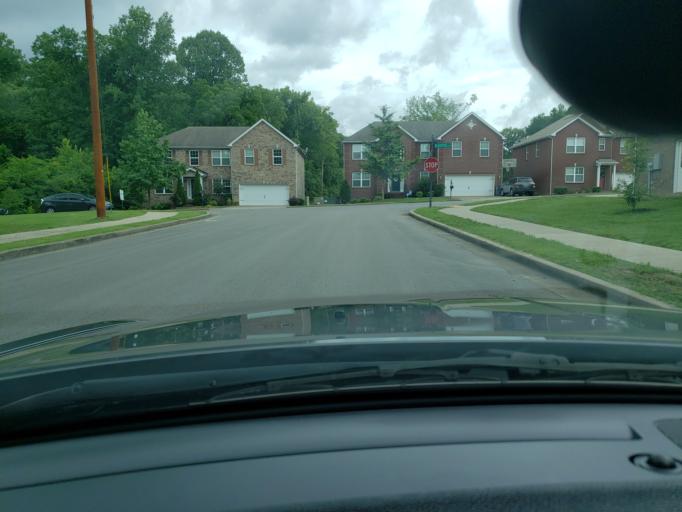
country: US
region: Tennessee
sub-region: Williamson County
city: Nolensville
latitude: 36.0214
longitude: -86.6900
